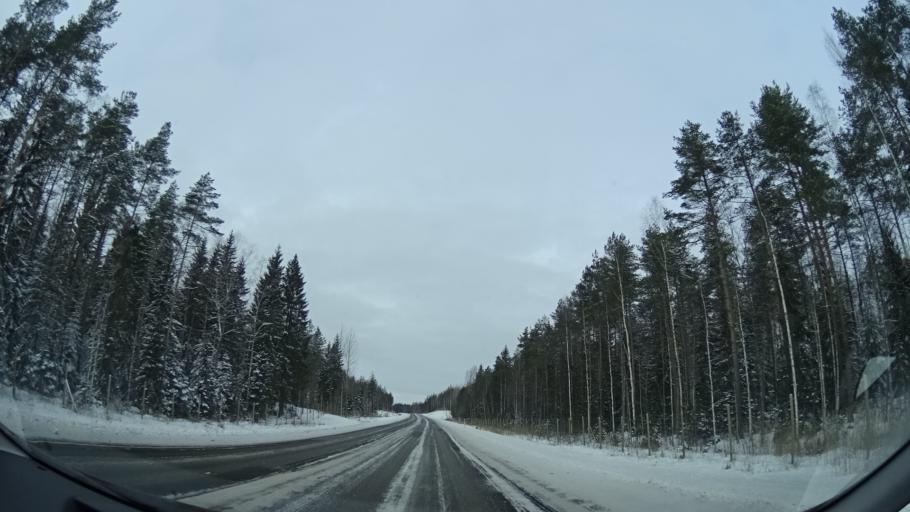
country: FI
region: Uusimaa
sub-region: Helsinki
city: Kaerkoelae
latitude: 60.6168
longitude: 24.0203
